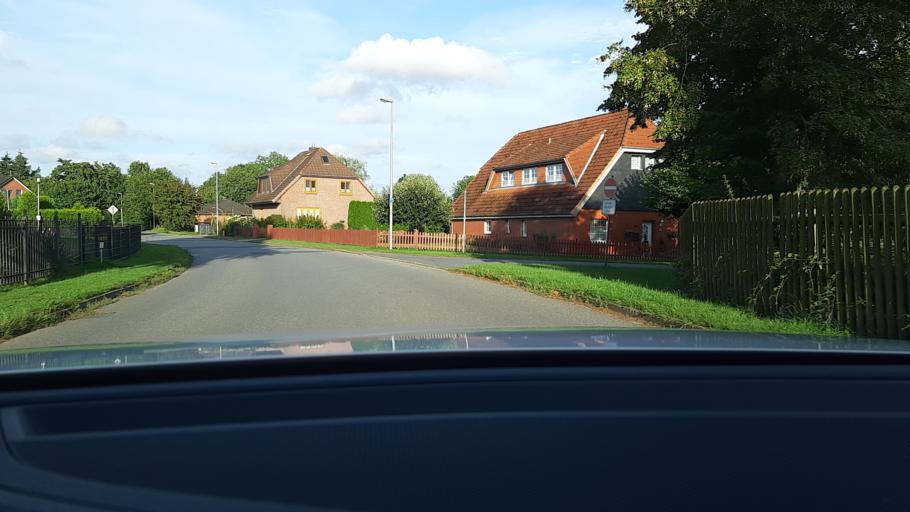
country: DE
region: Schleswig-Holstein
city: Monkhagen
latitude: 53.9263
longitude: 10.5733
